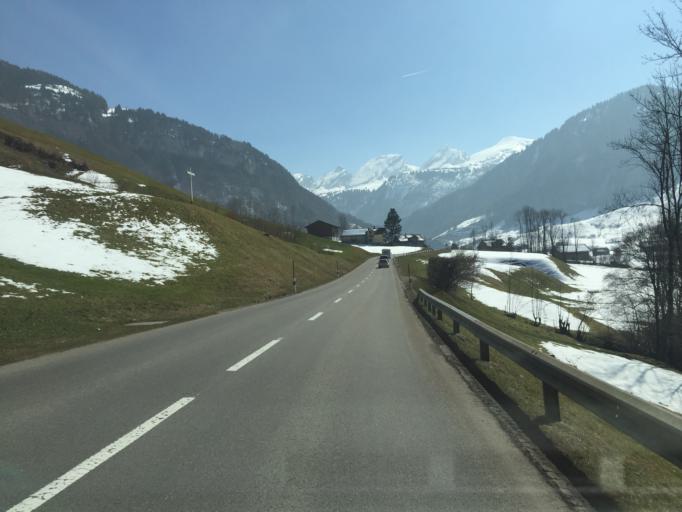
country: CH
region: Saint Gallen
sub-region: Wahlkreis Toggenburg
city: Krummenau
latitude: 47.2076
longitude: 9.2190
